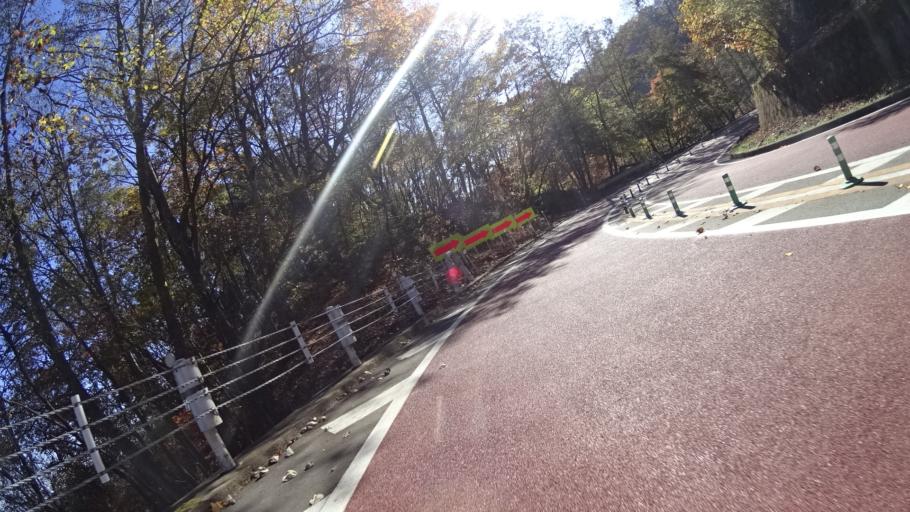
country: JP
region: Yamanashi
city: Uenohara
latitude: 35.7430
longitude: 139.0436
